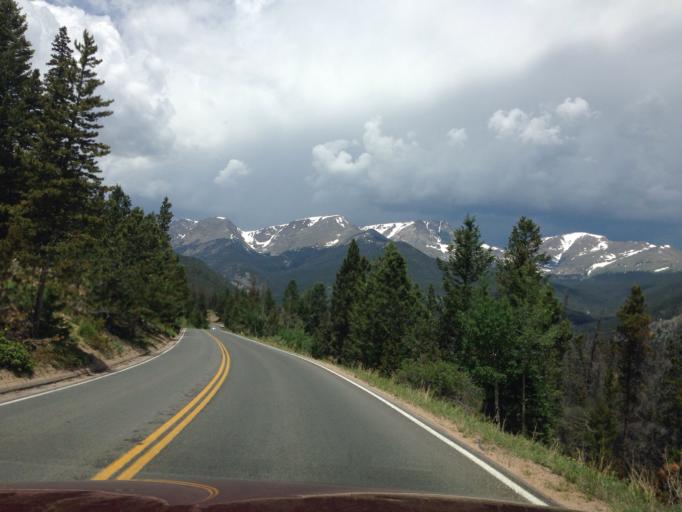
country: US
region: Colorado
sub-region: Larimer County
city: Estes Park
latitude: 40.3907
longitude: -105.6204
